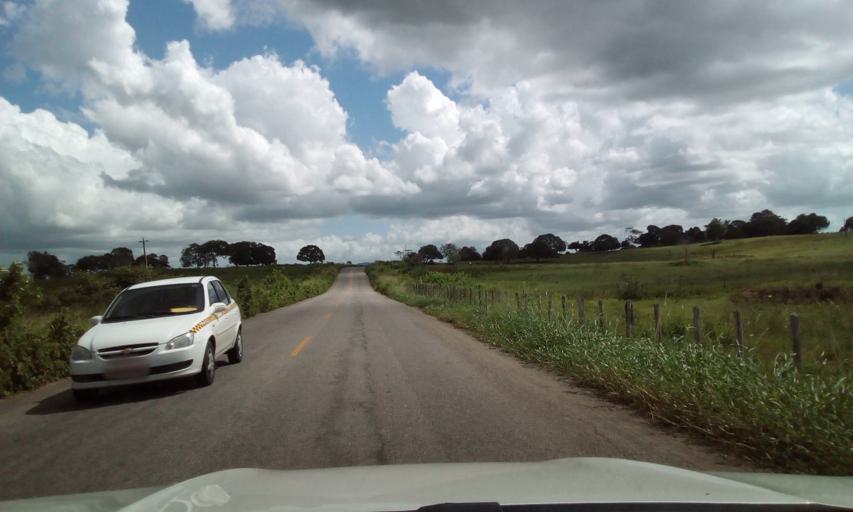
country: BR
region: Paraiba
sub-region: Guarabira
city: Guarabira
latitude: -6.8586
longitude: -35.4278
